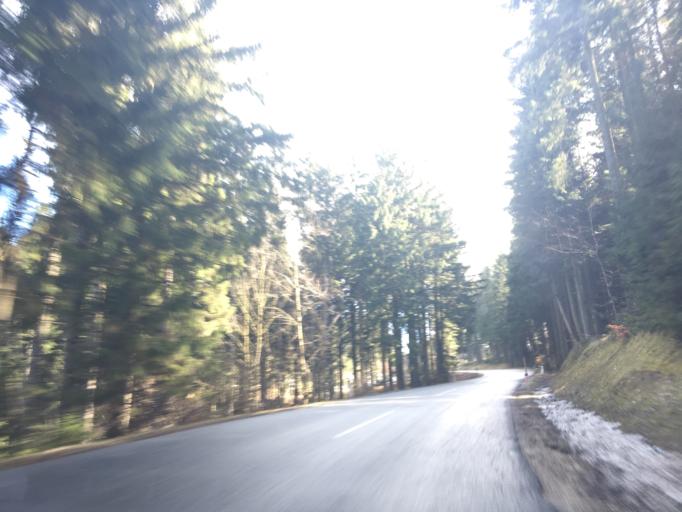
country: AT
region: Upper Austria
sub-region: Politischer Bezirk Perg
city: Sankt Georgen am Walde
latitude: 48.3806
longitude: 14.8969
